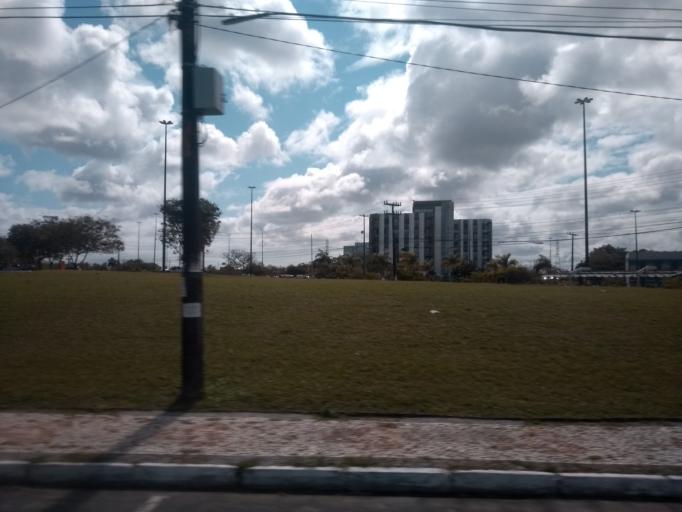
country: BR
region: Bahia
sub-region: Salvador
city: Salvador
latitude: -12.9441
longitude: -38.4270
